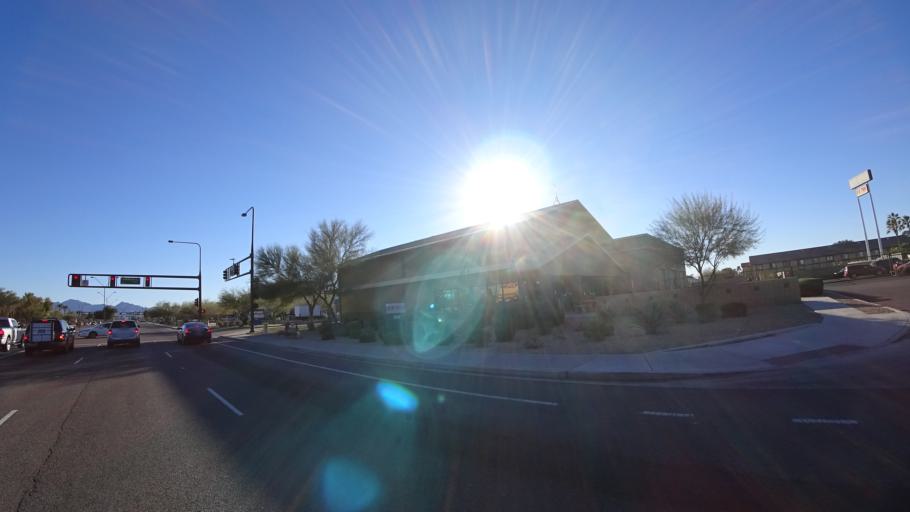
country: US
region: Arizona
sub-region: Maricopa County
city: Avondale
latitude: 33.4549
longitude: -112.3414
